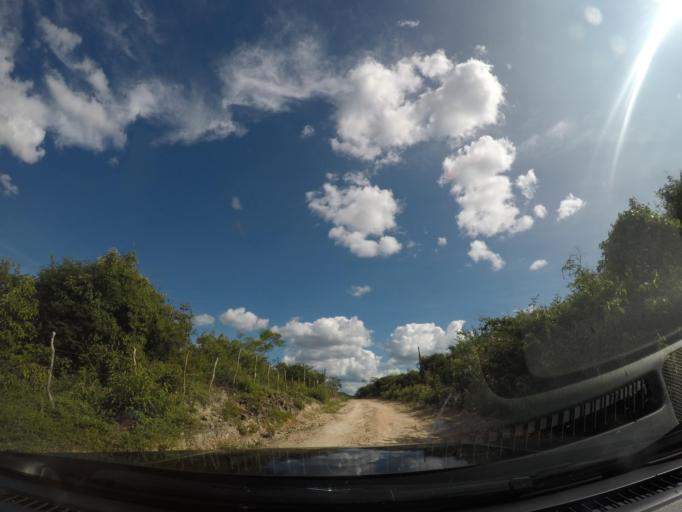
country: BR
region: Bahia
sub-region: Barra Da Estiva
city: Barra da Estiva
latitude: -13.2016
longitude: -41.5946
